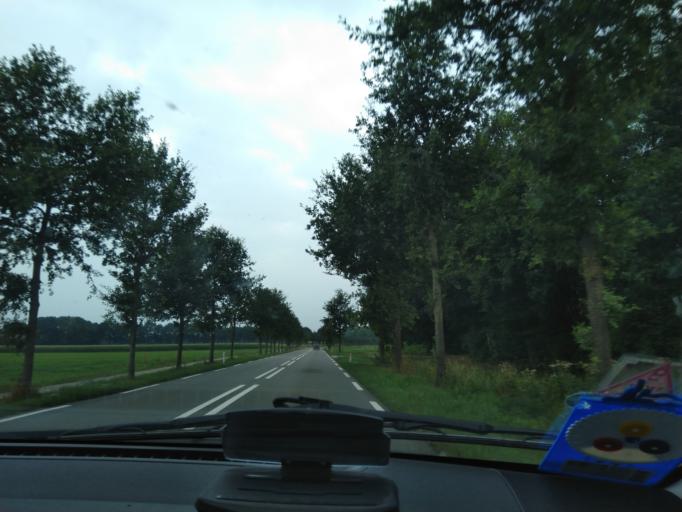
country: NL
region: Groningen
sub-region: Gemeente  Oldambt
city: Winschoten
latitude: 53.1138
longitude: 7.0501
